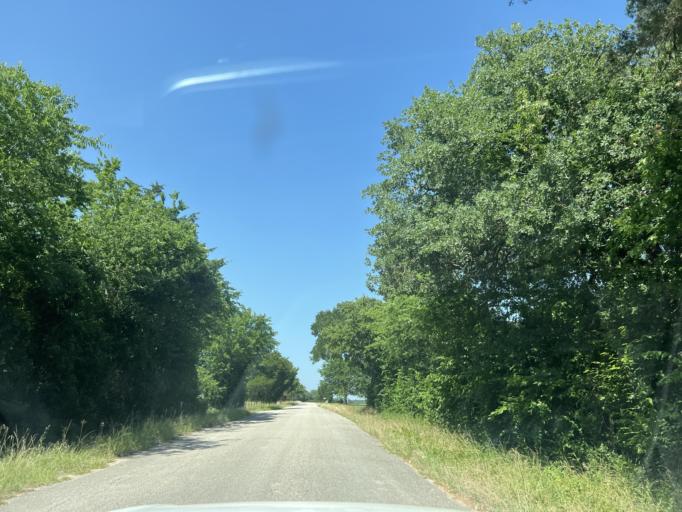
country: US
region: Texas
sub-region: Washington County
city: Brenham
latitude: 30.1655
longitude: -96.5203
